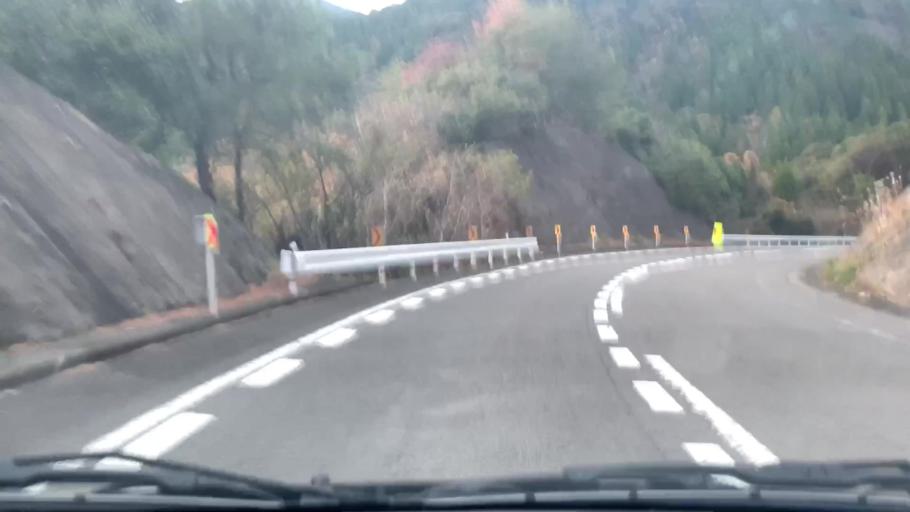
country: JP
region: Nagasaki
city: Omura
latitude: 32.9830
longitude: 130.0362
